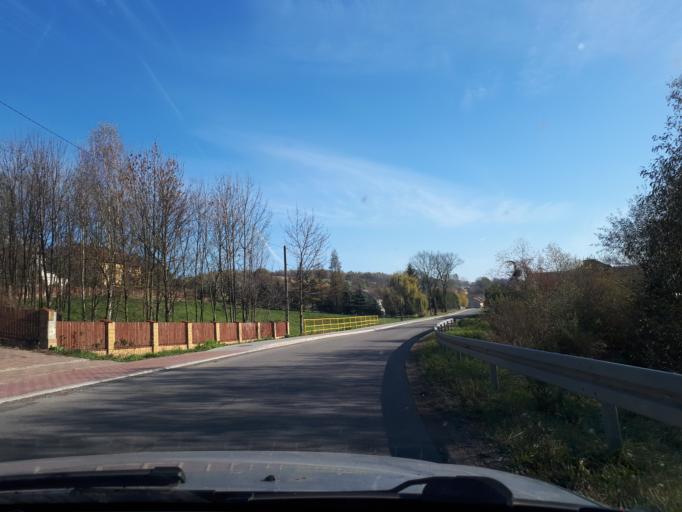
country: PL
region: Subcarpathian Voivodeship
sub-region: Powiat debicki
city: Debica
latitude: 50.0037
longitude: 21.4057
